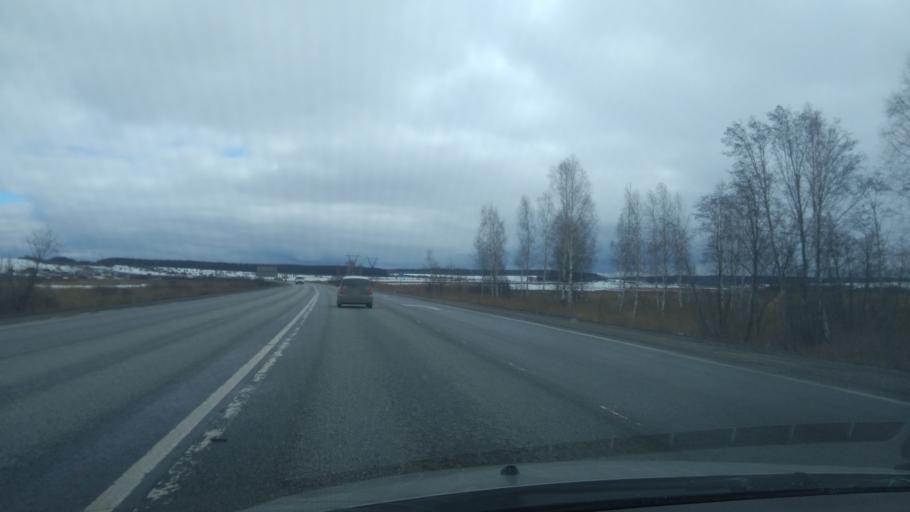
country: RU
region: Sverdlovsk
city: Achit
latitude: 56.7863
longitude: 57.8881
